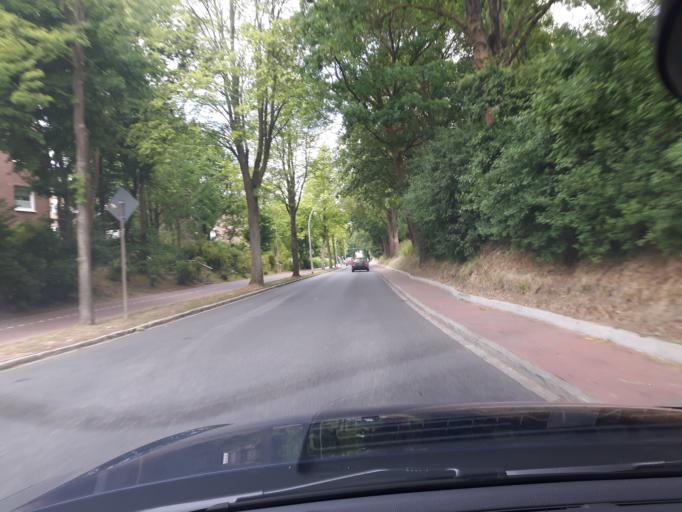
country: DE
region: Schleswig-Holstein
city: Neustadt in Holstein
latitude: 54.0944
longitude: 10.8242
